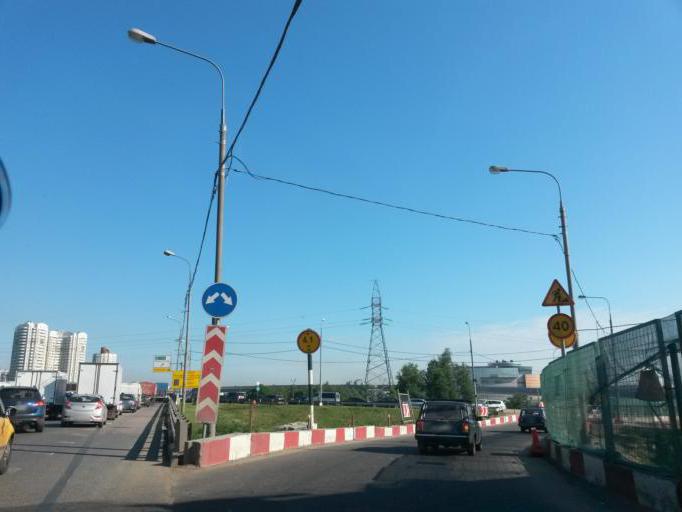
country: RU
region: Moskovskaya
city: Razvilka
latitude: 55.5904
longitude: 37.7311
